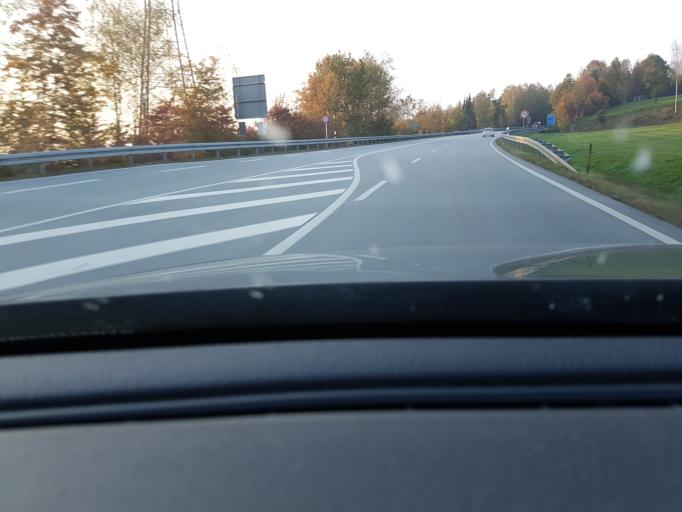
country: DE
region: Bavaria
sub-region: Lower Bavaria
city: Tiefenbach
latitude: 48.6007
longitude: 13.3701
